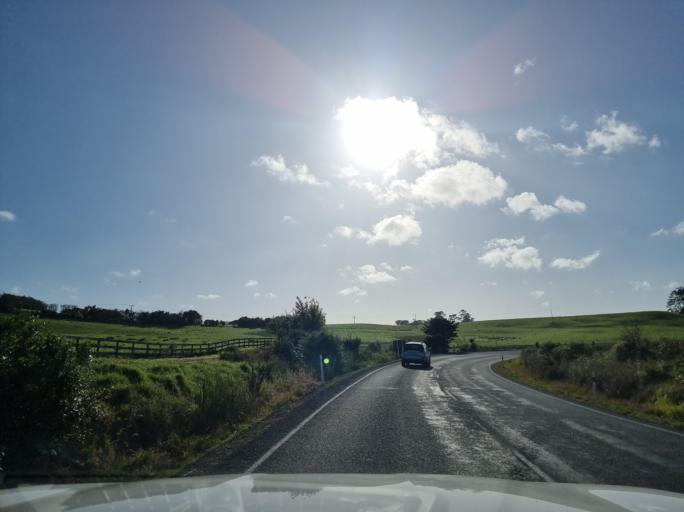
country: NZ
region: Northland
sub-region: Whangarei
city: Ruakaka
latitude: -35.9903
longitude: 174.4593
